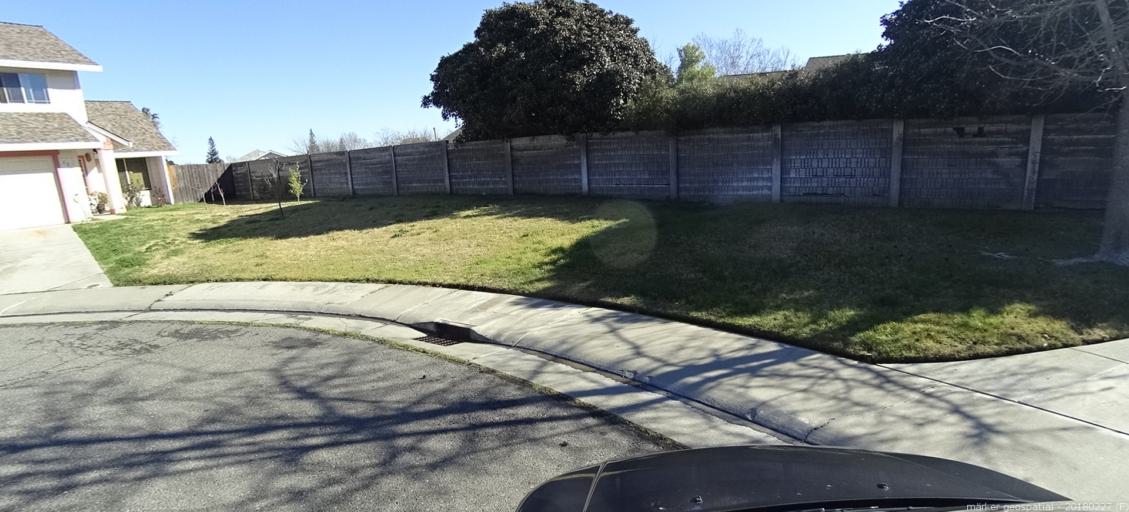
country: US
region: California
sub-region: Sacramento County
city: North Highlands
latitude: 38.7192
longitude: -121.3670
